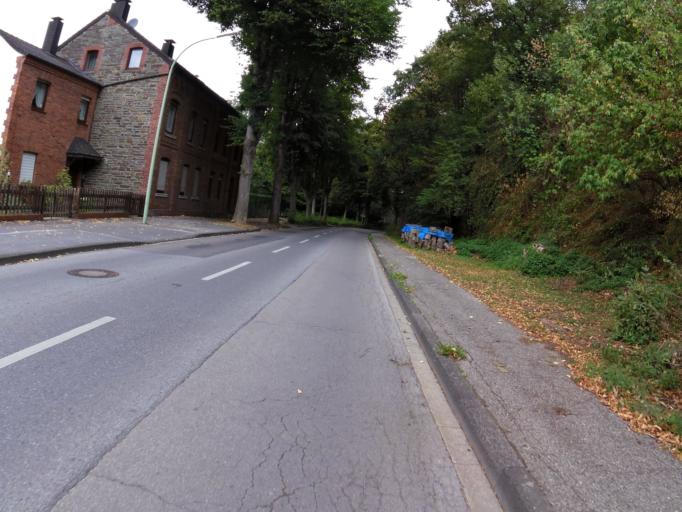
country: DE
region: North Rhine-Westphalia
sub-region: Regierungsbezirk Koln
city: Langerwehe
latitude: 50.7643
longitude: 6.3280
